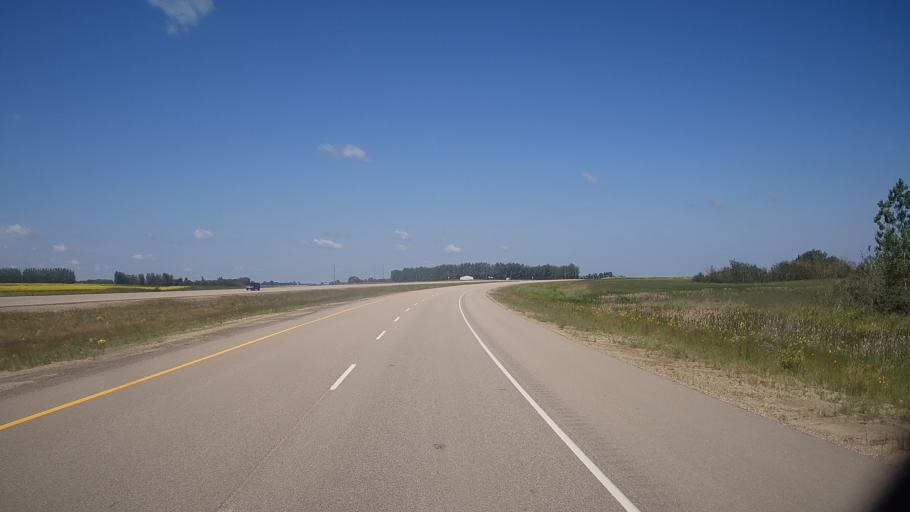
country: CA
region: Saskatchewan
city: Saskatoon
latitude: 51.9982
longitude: -106.3206
